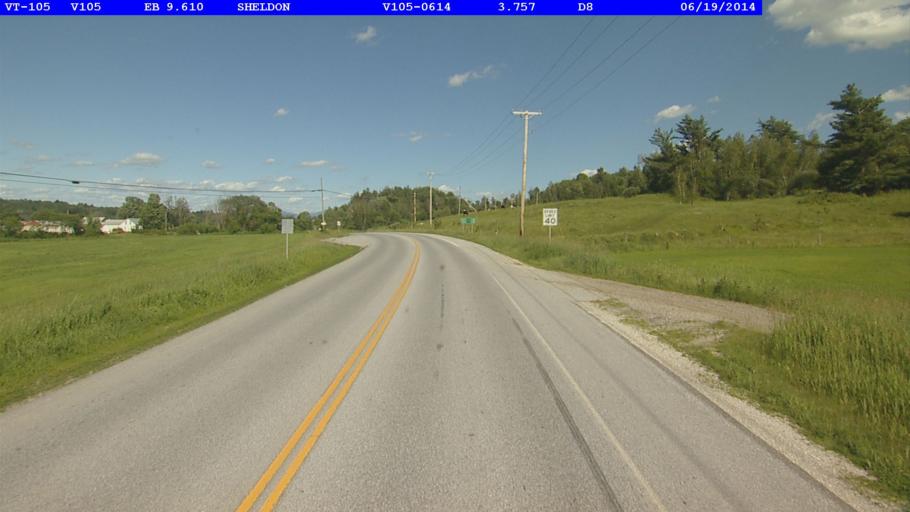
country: US
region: Vermont
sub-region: Franklin County
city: Enosburg Falls
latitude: 44.8999
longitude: -72.9581
